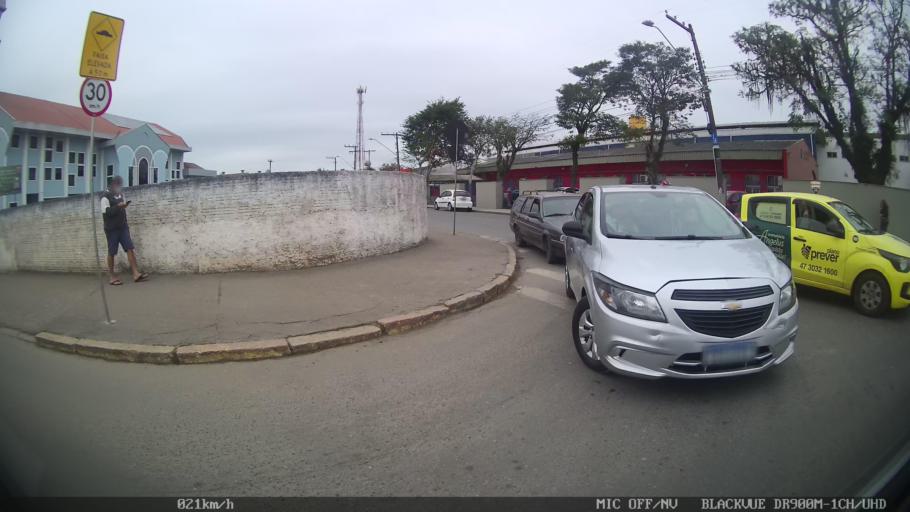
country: BR
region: Santa Catarina
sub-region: Joinville
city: Joinville
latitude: -26.3404
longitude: -48.8145
